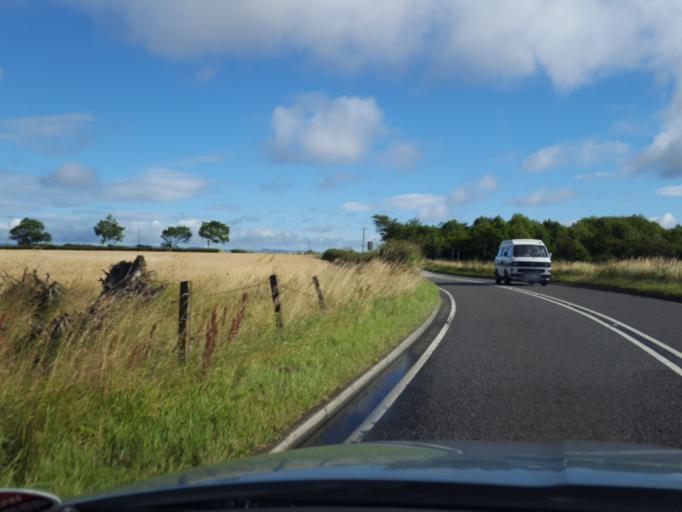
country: GB
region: Scotland
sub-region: West Lothian
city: Broxburn
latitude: 55.9524
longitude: -3.5101
